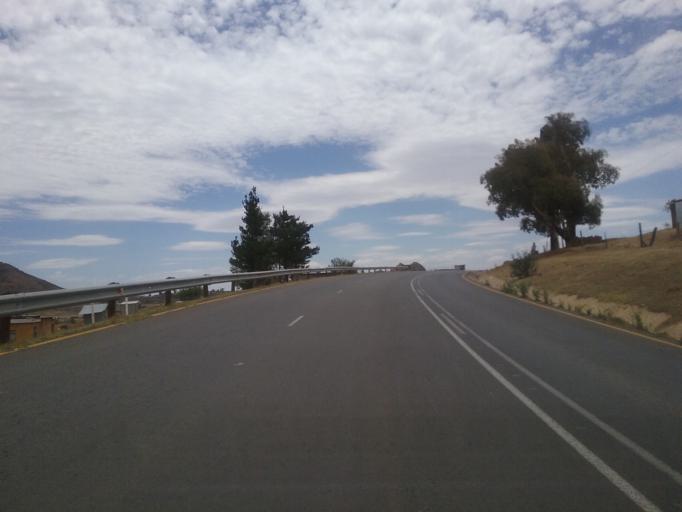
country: LS
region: Maseru
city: Maseru
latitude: -29.5107
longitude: 27.5231
